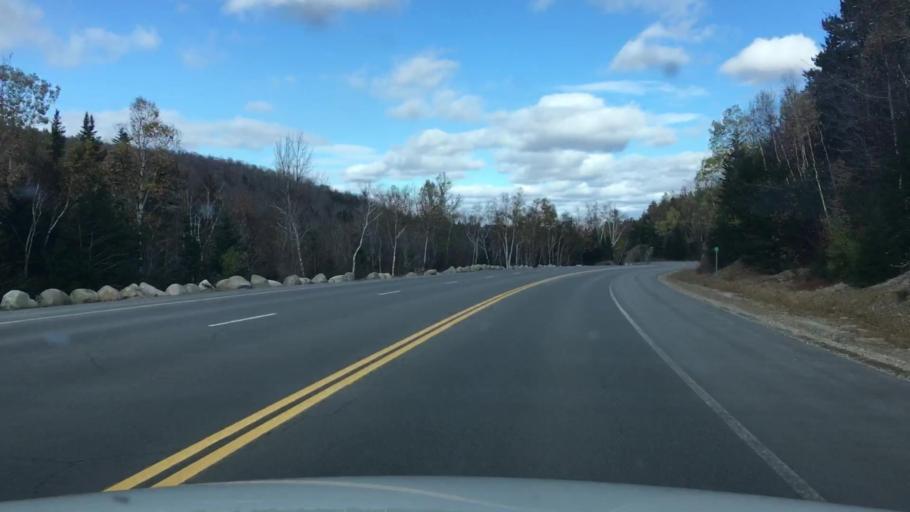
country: US
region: New Hampshire
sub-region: Coos County
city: Gorham
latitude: 44.2792
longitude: -71.2320
